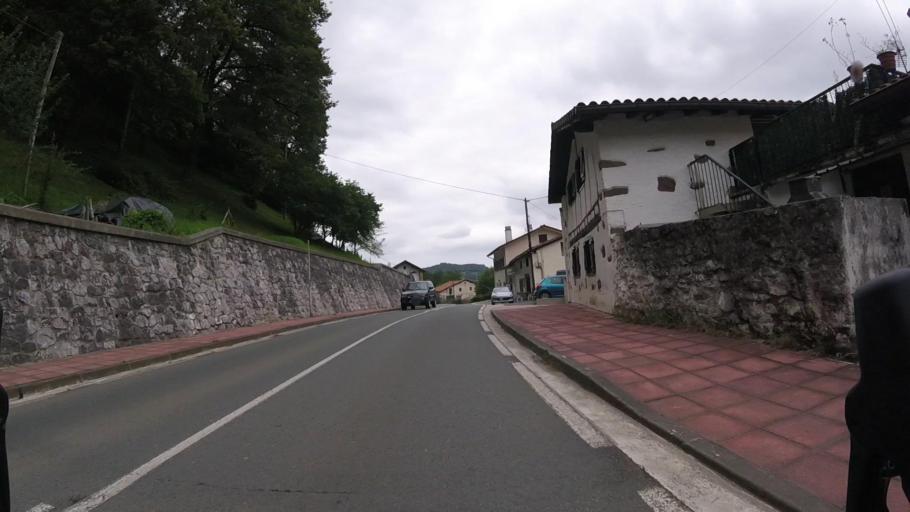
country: ES
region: Basque Country
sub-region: Provincia de Guipuzcoa
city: Irun
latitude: 43.2868
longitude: -1.8350
